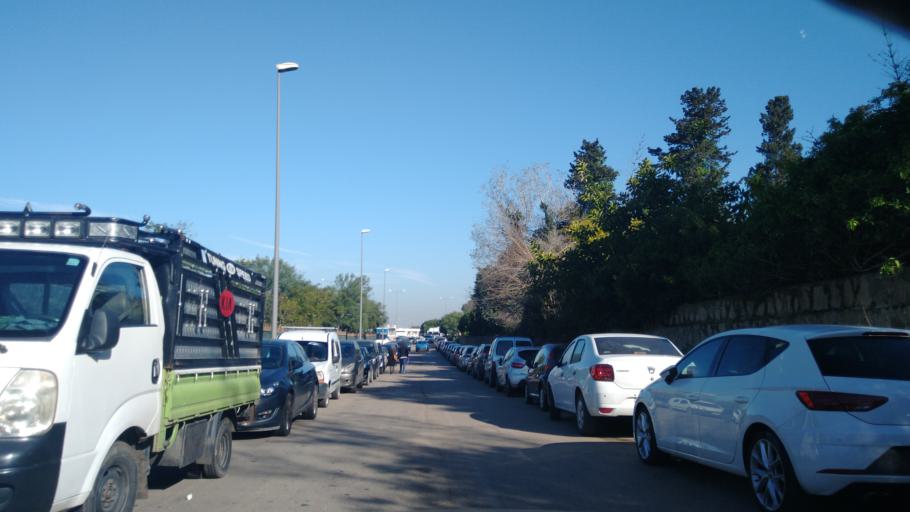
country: MA
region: Rabat-Sale-Zemmour-Zaer
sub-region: Rabat
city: Rabat
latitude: 33.9824
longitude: -6.8536
